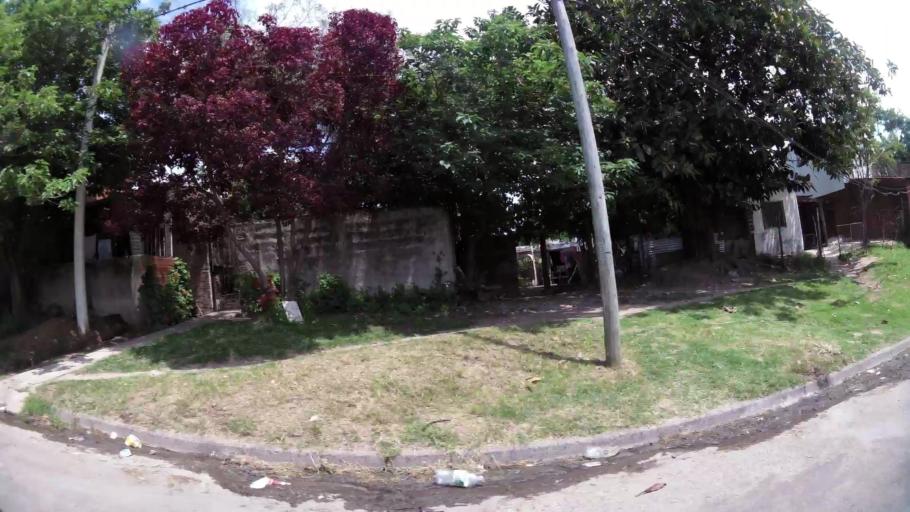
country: AR
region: Santa Fe
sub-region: Departamento de Rosario
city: Rosario
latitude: -32.9822
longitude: -60.6259
